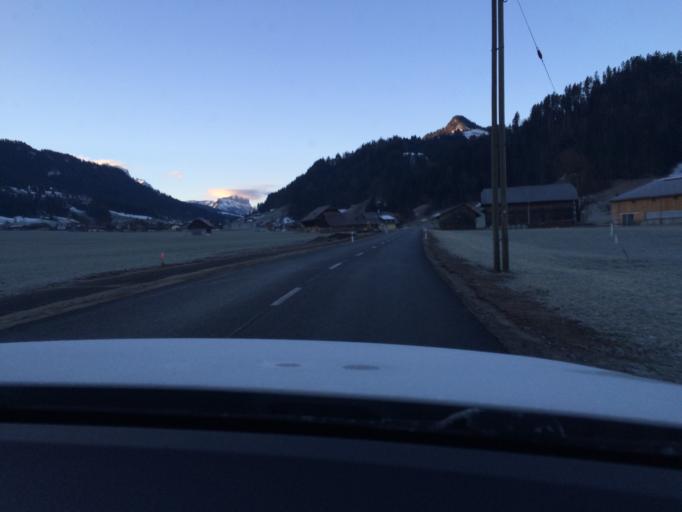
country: CH
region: Lucerne
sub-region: Entlebuch District
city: Escholzmatt
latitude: 46.8649
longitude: 7.9054
